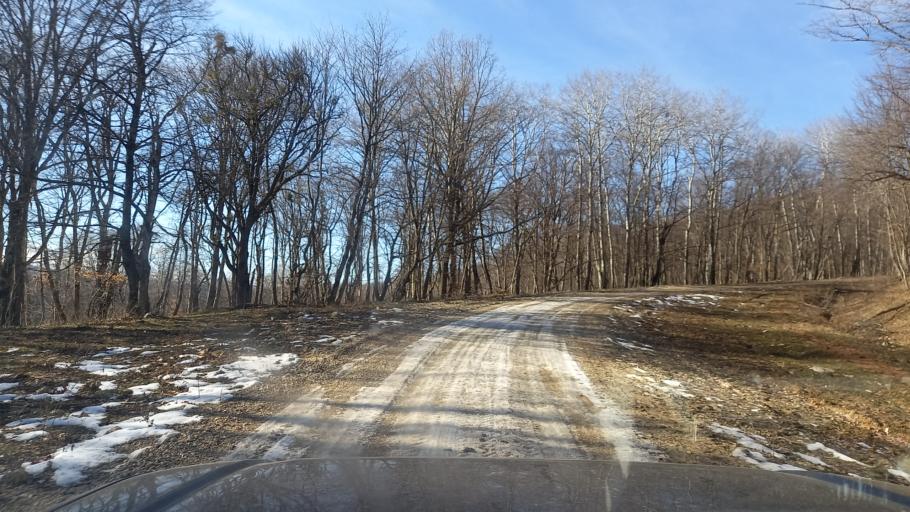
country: RU
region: Adygeya
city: Kamennomostskiy
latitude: 44.2828
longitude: 40.3189
